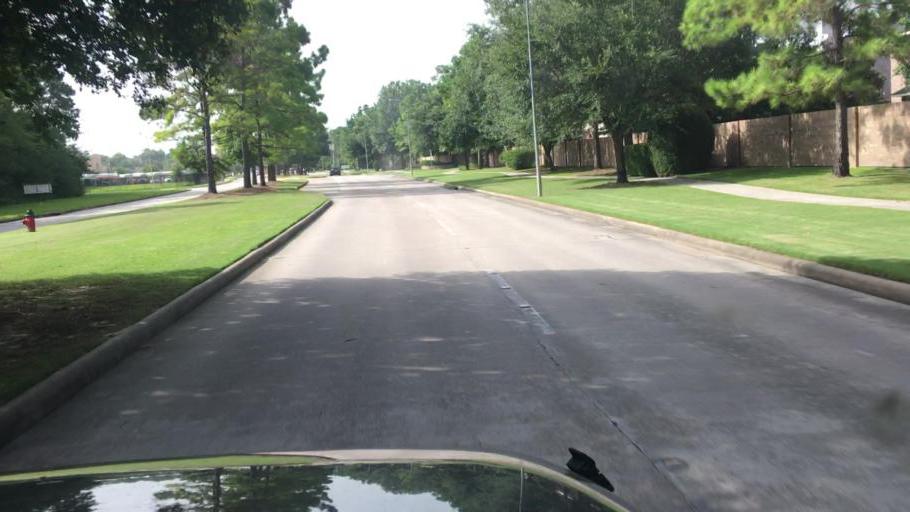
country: US
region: Texas
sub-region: Harris County
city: Atascocita
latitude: 29.9846
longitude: -95.1909
